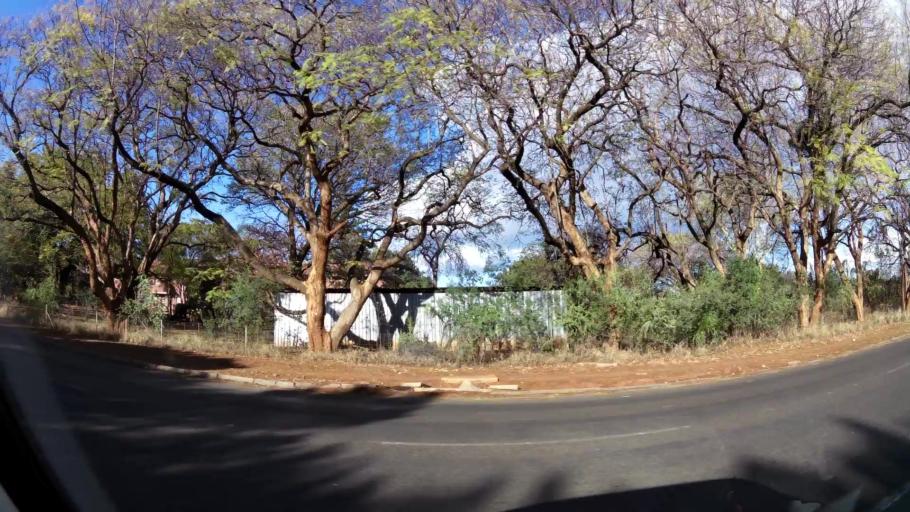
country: ZA
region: Limpopo
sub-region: Waterberg District Municipality
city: Mokopane
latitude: -24.1951
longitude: 29.0087
